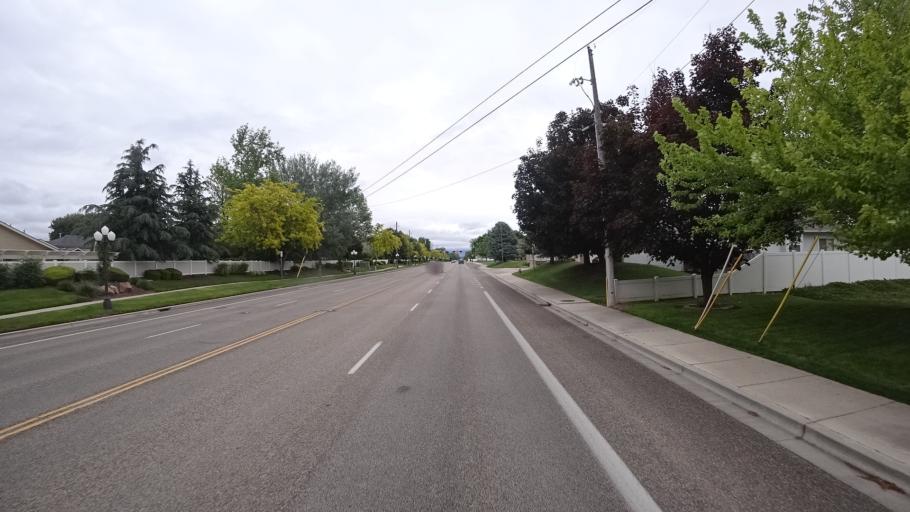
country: US
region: Idaho
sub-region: Ada County
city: Eagle
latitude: 43.6485
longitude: -116.3270
